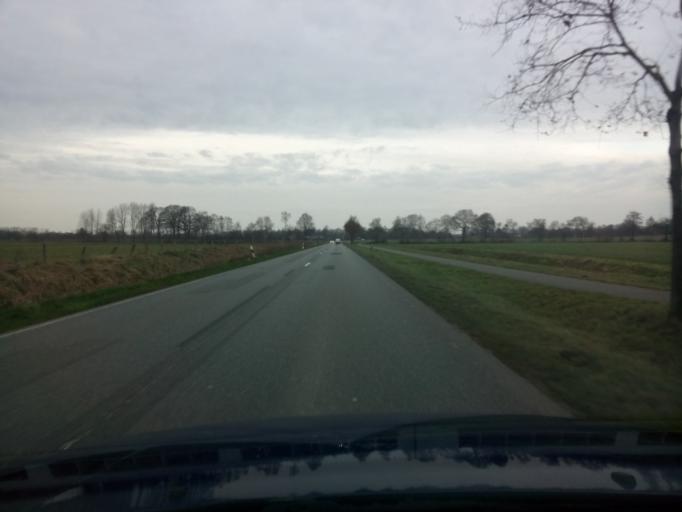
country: DE
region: Lower Saxony
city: Kuhrstedt
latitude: 53.6163
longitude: 8.8211
